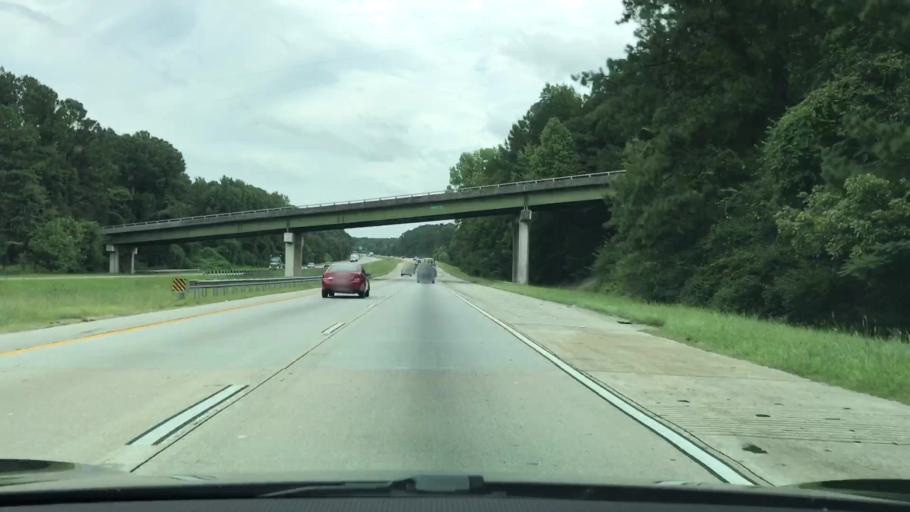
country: US
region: Georgia
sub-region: Coweta County
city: Grantville
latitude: 33.2143
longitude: -84.8222
